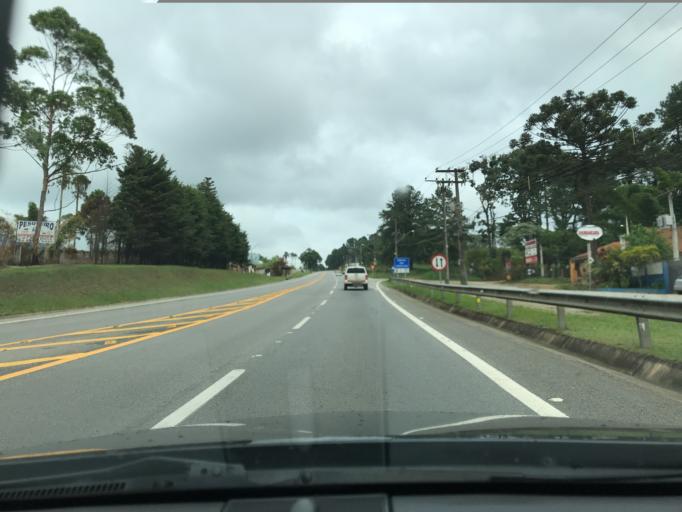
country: BR
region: Sao Paulo
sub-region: Vargem Grande Paulista
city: Vargem Grande Paulista
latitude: -23.5987
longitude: -47.0411
